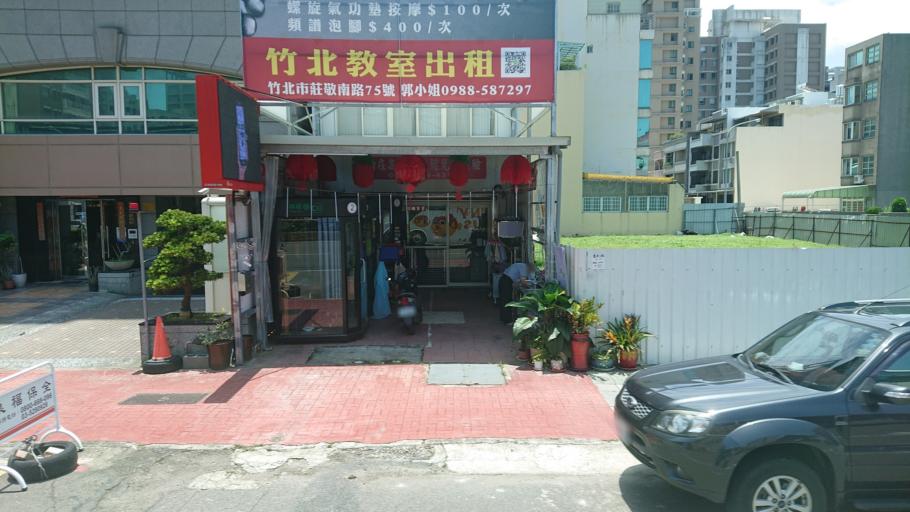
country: TW
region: Taiwan
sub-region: Hsinchu
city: Zhubei
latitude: 24.8177
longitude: 121.0209
